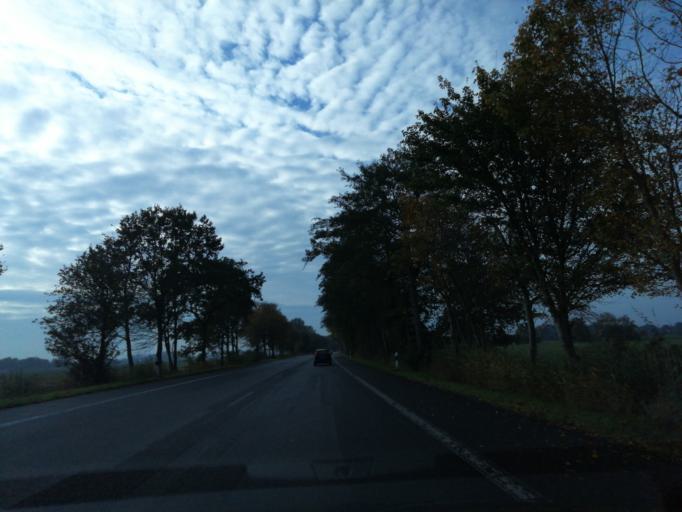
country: DE
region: Lower Saxony
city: Fedderwarden
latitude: 53.5703
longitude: 8.0559
